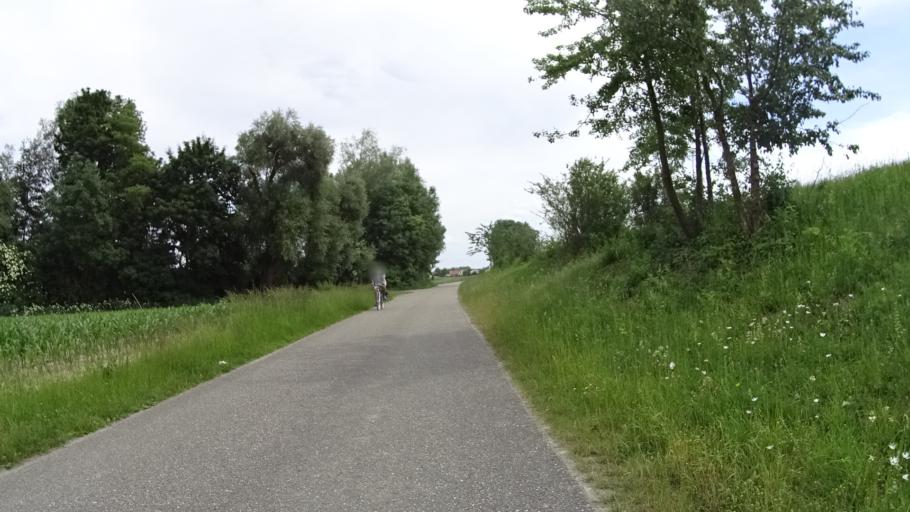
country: DE
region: Bavaria
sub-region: Upper Palatinate
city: Donaustauf
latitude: 49.0194
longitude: 12.2609
